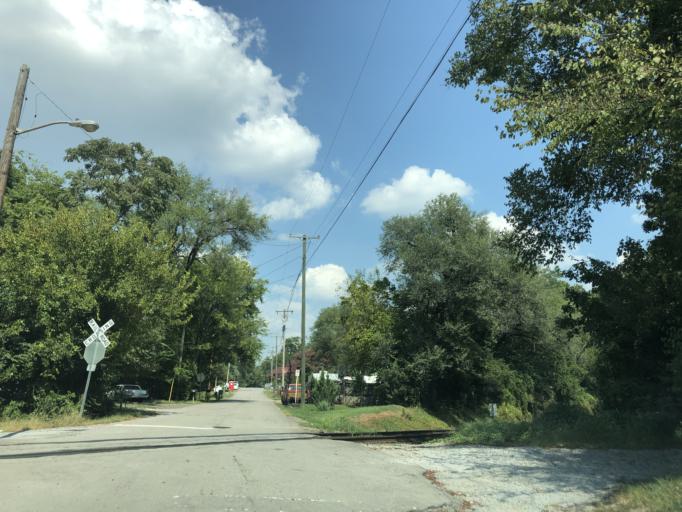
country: US
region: Tennessee
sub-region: Davidson County
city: Oak Hill
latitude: 36.1269
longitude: -86.7475
